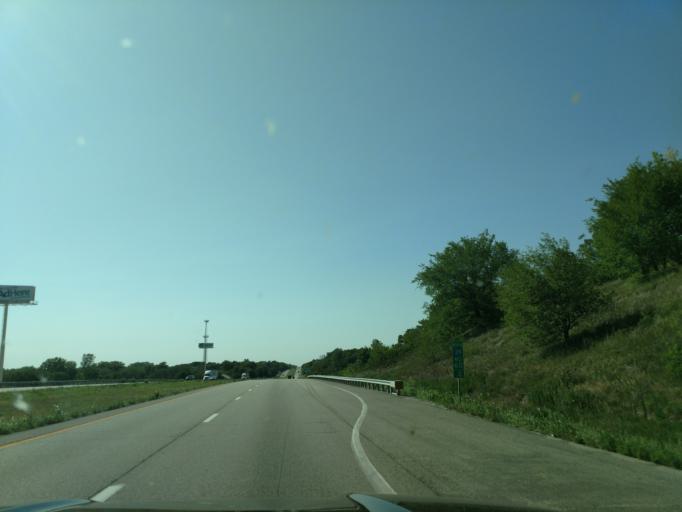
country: US
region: Missouri
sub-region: Andrew County
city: Savannah
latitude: 39.9165
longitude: -94.9050
